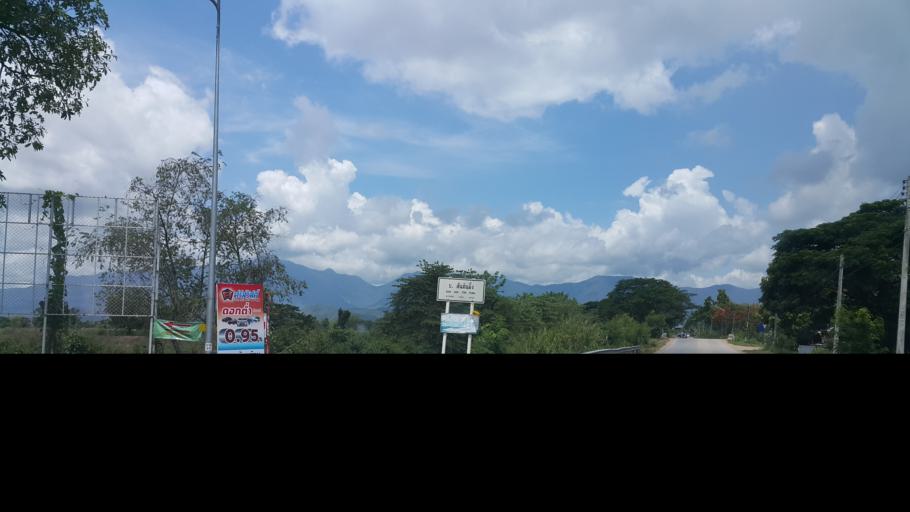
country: TH
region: Phayao
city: Phayao
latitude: 19.2018
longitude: 99.8629
